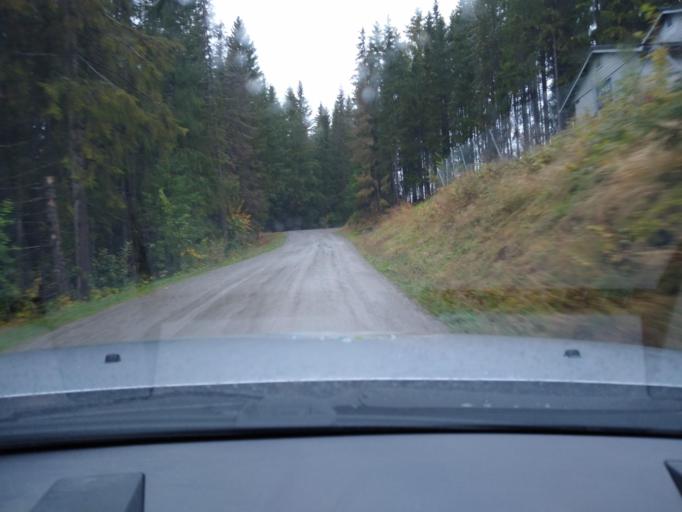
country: NO
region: Oppland
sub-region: Ringebu
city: Ringebu
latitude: 61.5396
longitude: 10.1492
